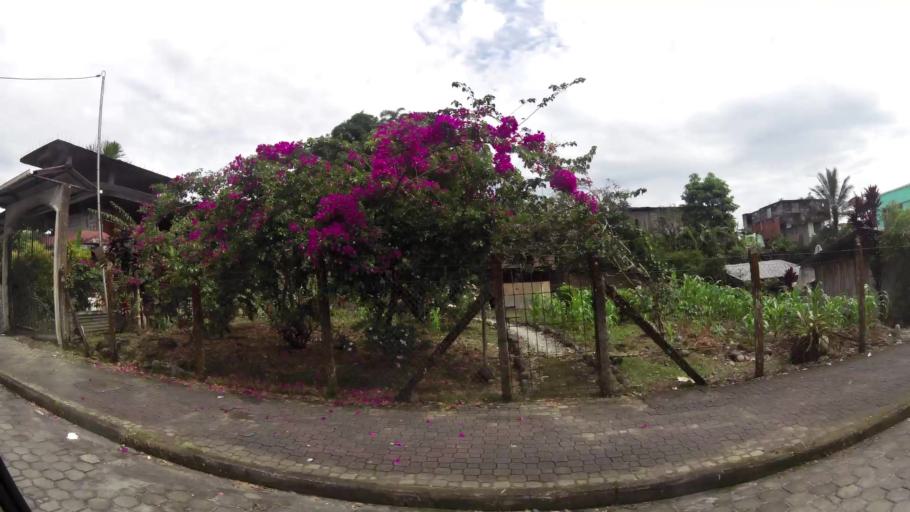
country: EC
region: Pastaza
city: Puyo
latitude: -1.4969
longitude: -78.0004
